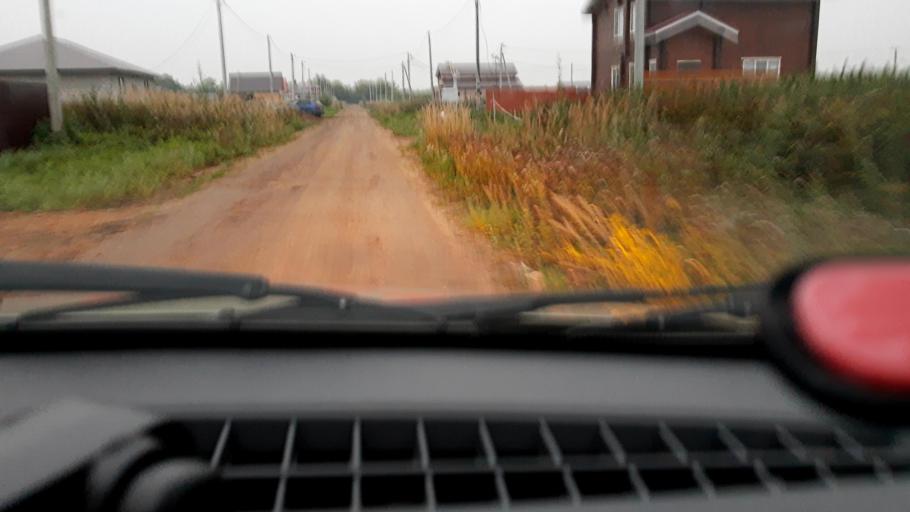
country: RU
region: Bashkortostan
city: Kabakovo
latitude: 54.5787
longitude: 56.2817
